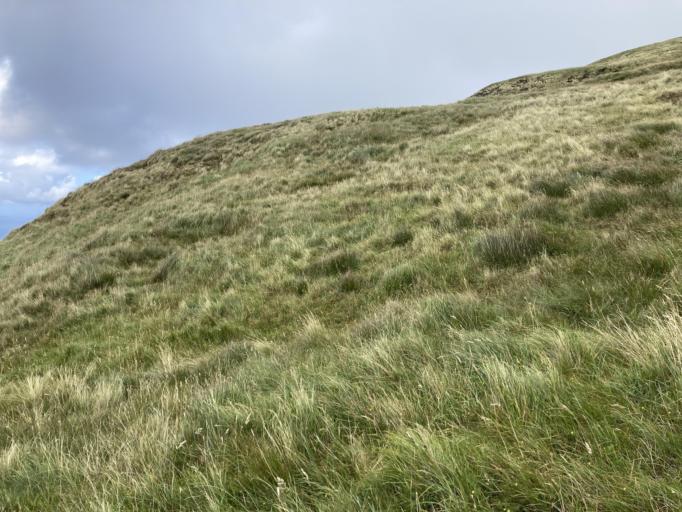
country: GB
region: Scotland
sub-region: Highland
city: Isle of Skye
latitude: 57.0195
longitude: -6.4010
